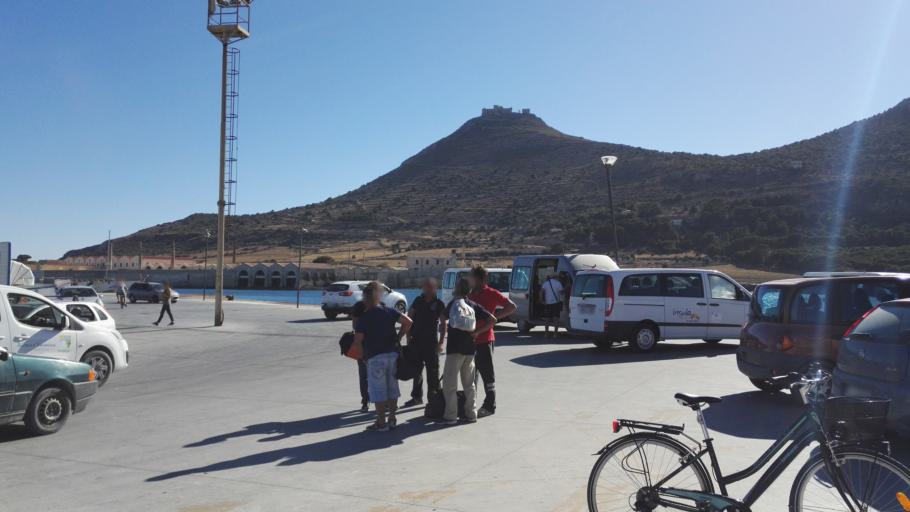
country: IT
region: Sicily
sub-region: Trapani
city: Favignana
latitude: 37.9332
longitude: 12.3258
